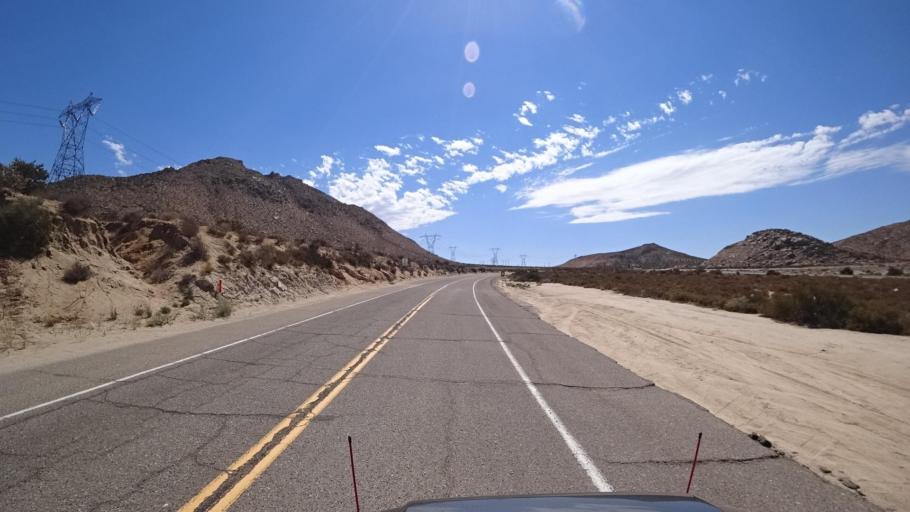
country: MX
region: Baja California
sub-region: Tecate
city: Cereso del Hongo
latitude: 32.6420
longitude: -116.1063
